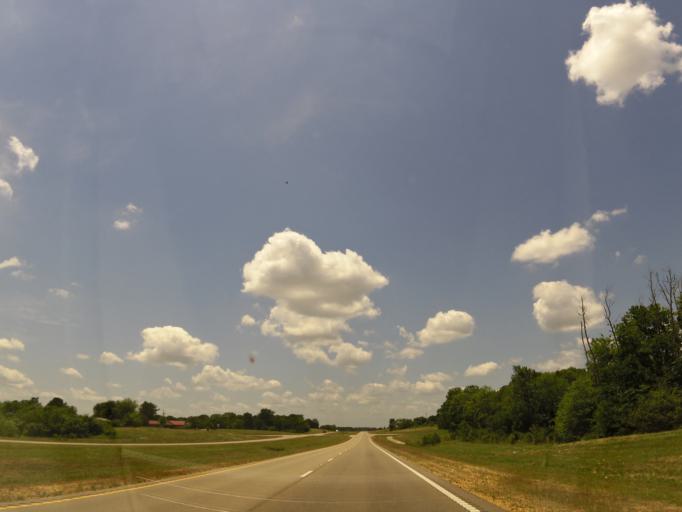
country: US
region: Mississippi
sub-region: Lee County
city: Verona
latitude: 34.2134
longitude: -88.7949
